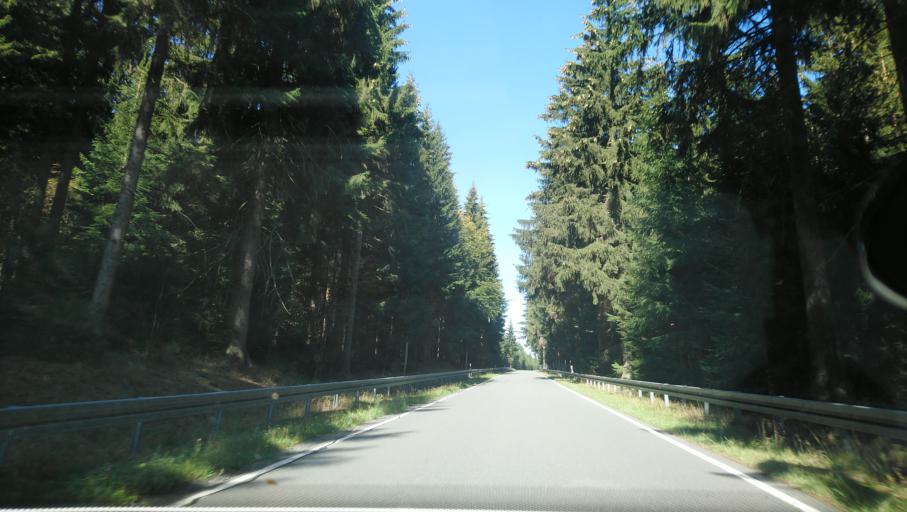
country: DE
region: Saxony
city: Barenstein
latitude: 50.5024
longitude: 13.0552
